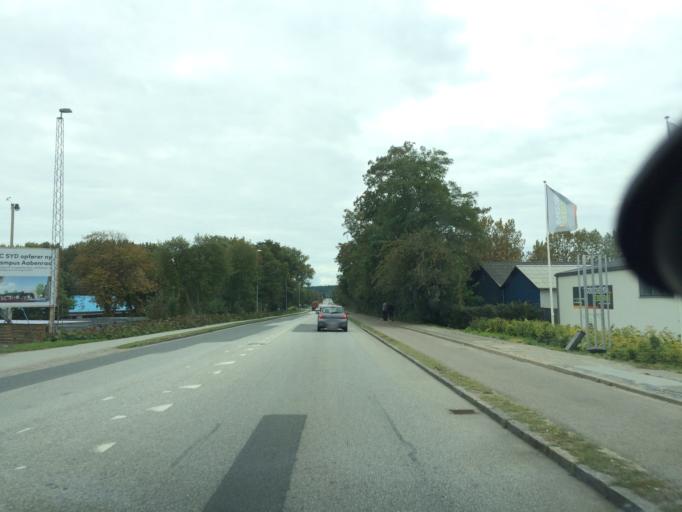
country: DK
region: South Denmark
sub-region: Aabenraa Kommune
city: Aabenraa
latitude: 55.0444
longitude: 9.4046
